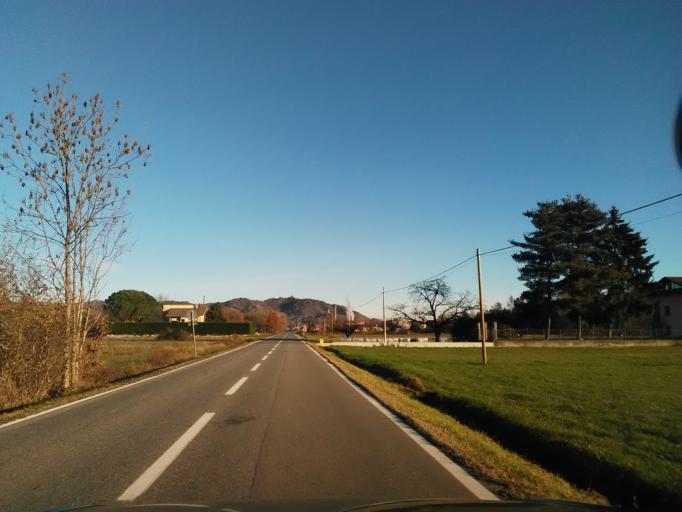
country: IT
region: Piedmont
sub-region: Provincia di Vercelli
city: Gattinara
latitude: 45.5991
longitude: 8.3481
